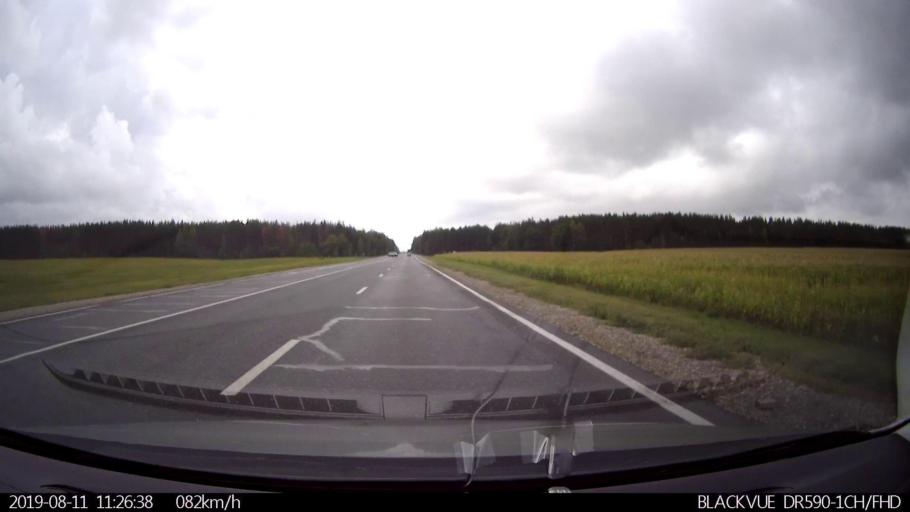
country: RU
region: Ulyanovsk
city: Krasnyy Gulyay
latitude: 54.1029
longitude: 48.2344
